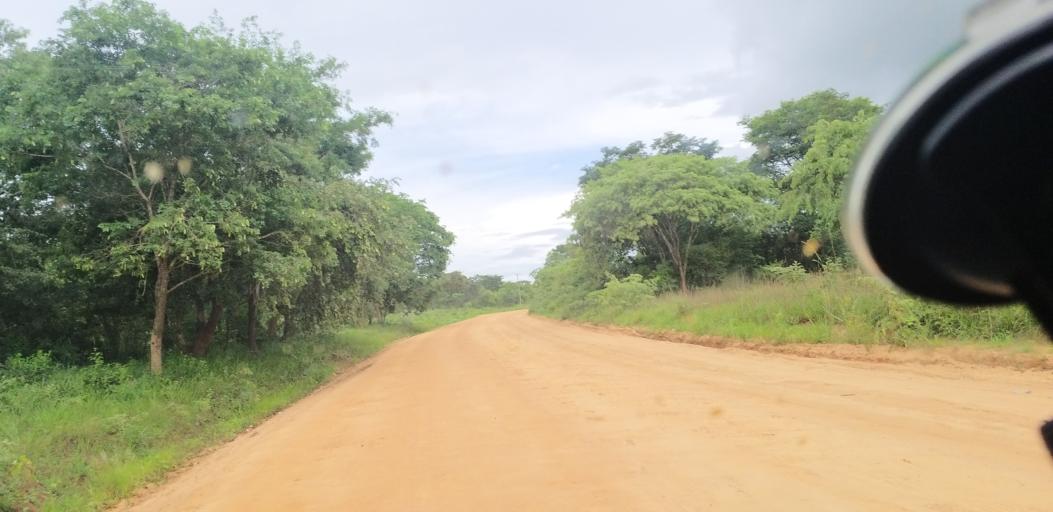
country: ZM
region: Lusaka
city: Chongwe
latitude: -15.1806
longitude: 28.4508
